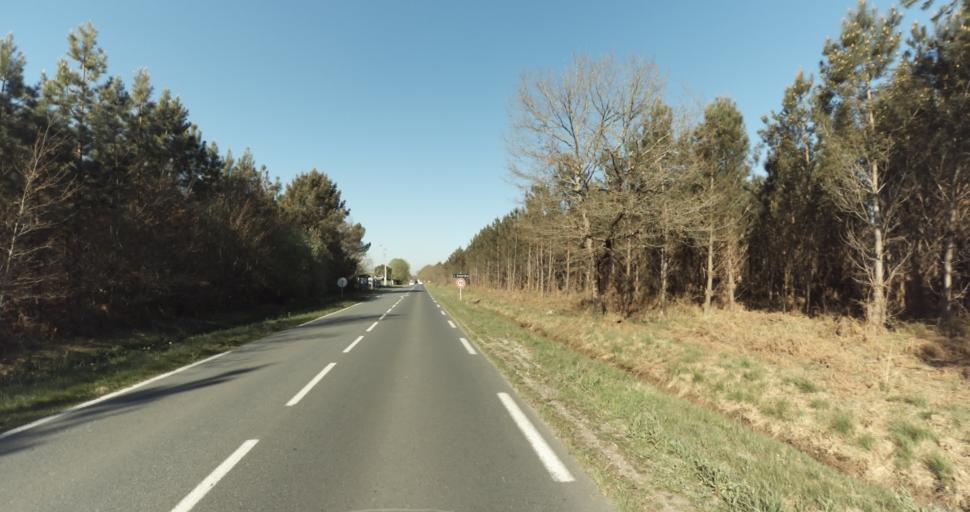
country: FR
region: Aquitaine
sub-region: Departement de la Gironde
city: Martignas-sur-Jalle
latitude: 44.7945
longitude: -0.8613
